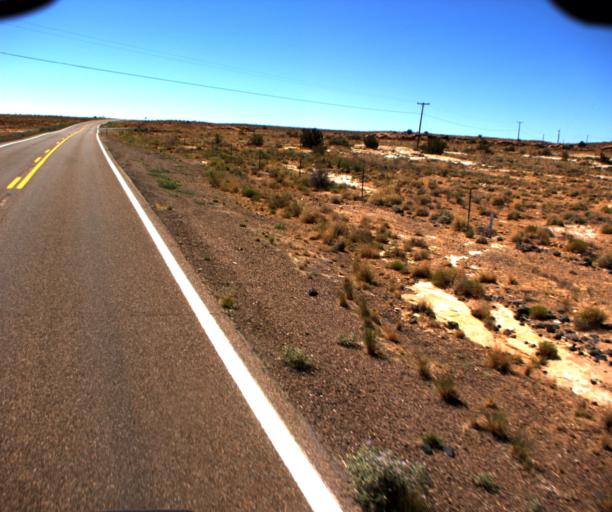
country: US
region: Arizona
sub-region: Navajo County
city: Winslow
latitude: 34.9752
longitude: -110.6527
